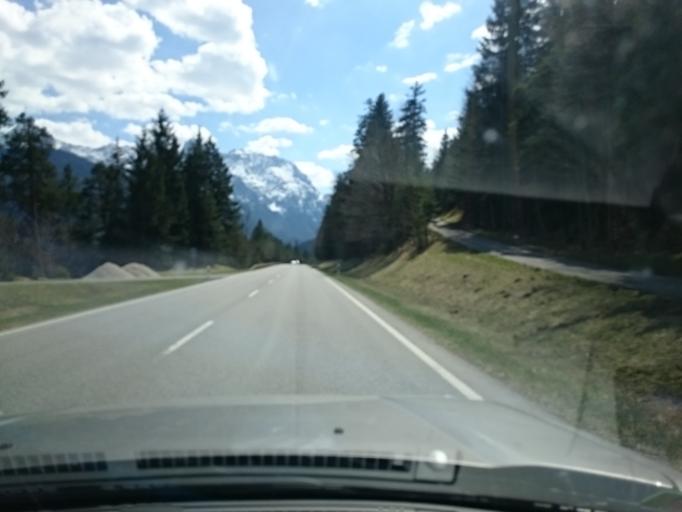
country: DE
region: Bavaria
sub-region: Upper Bavaria
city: Krun
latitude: 47.4876
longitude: 11.2745
